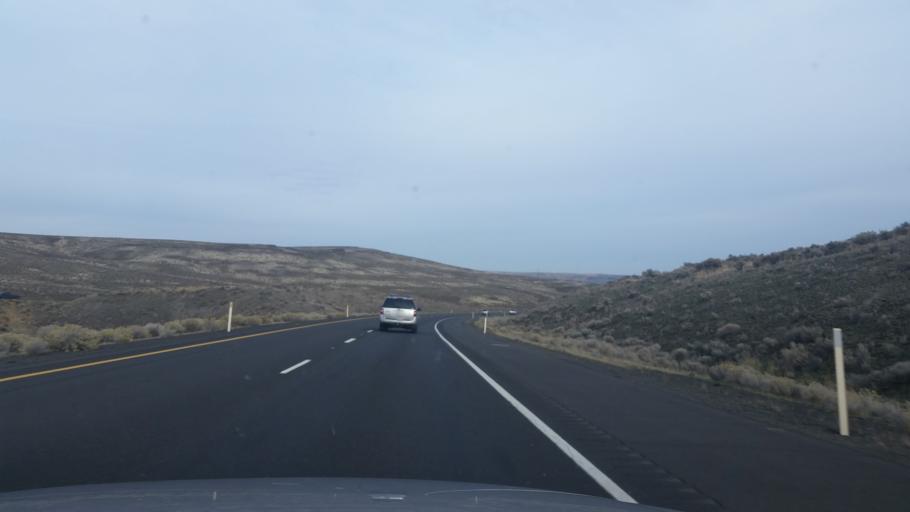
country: US
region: Washington
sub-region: Grant County
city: Mattawa
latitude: 46.9376
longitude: -120.0309
